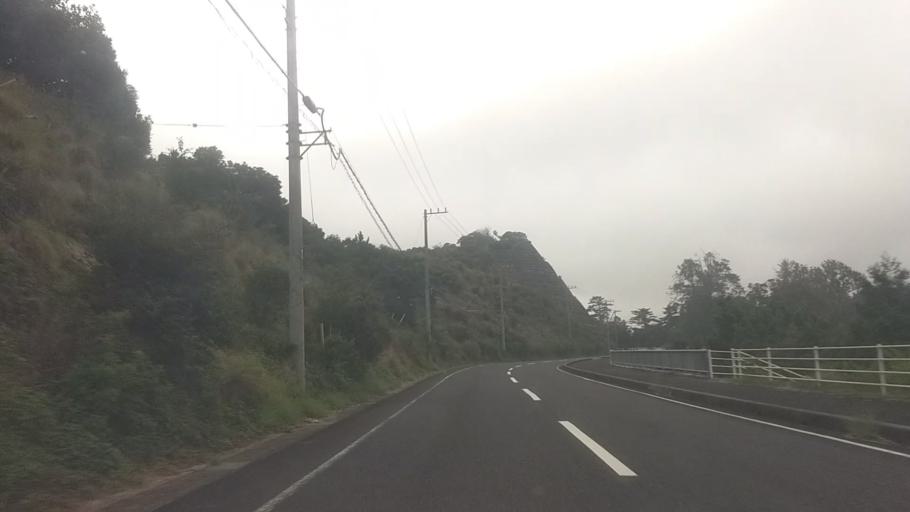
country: JP
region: Chiba
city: Kawaguchi
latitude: 35.1468
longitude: 140.1499
